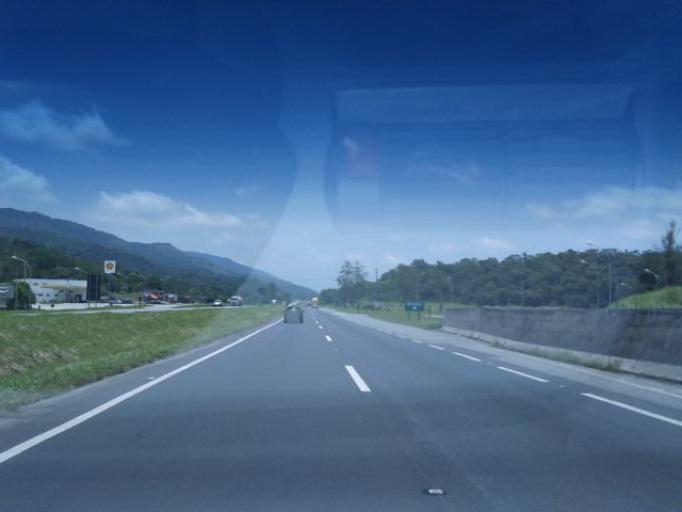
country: BR
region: Sao Paulo
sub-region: Miracatu
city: Miracatu
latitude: -24.2722
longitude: -47.4052
